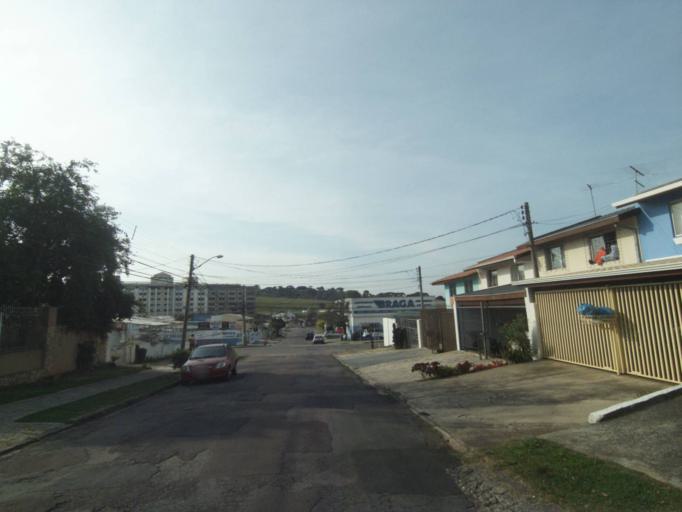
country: BR
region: Parana
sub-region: Curitiba
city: Curitiba
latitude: -25.4587
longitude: -49.3146
